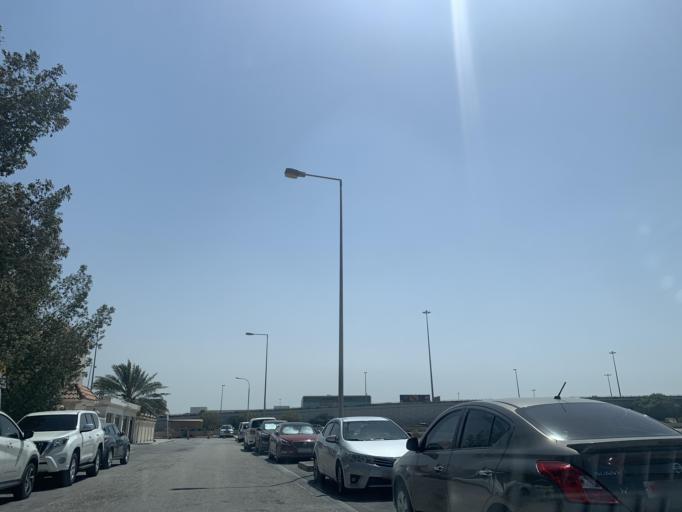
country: BH
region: Manama
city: Manama
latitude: 26.2060
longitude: 50.5698
